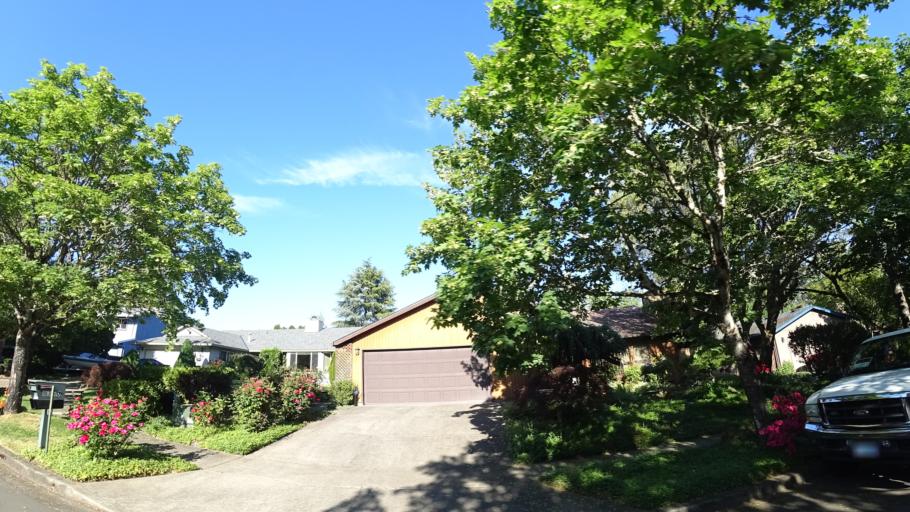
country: US
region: Oregon
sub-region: Washington County
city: Beaverton
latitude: 45.4592
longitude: -122.8112
